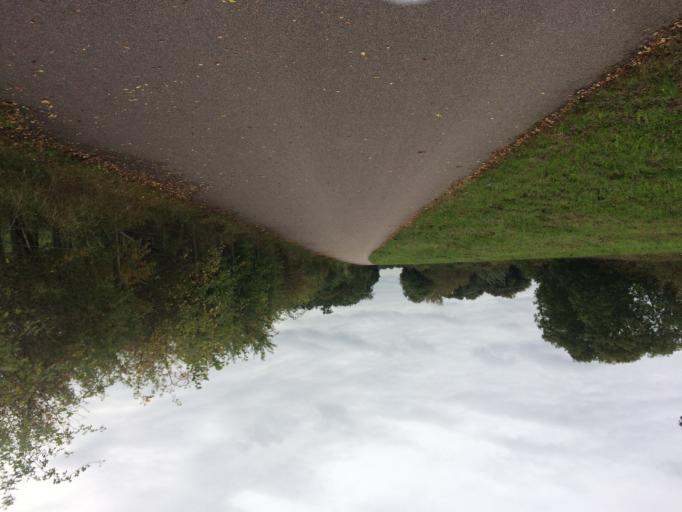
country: GB
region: England
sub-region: Cambridgeshire
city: Histon
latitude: 52.2649
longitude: 0.0773
